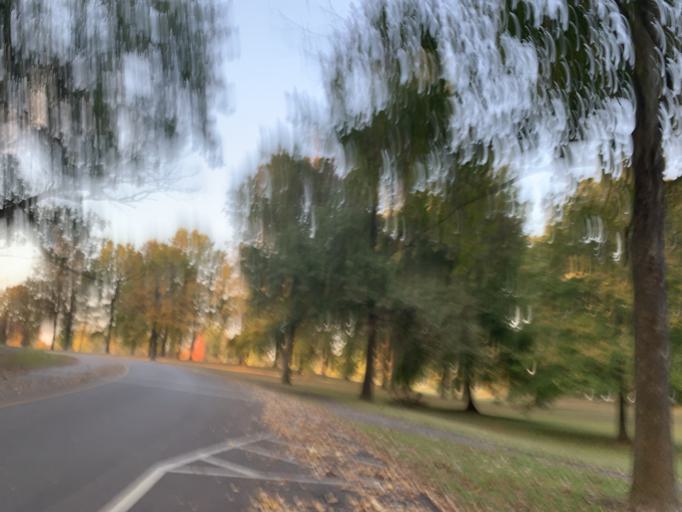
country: US
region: Indiana
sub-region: Floyd County
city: New Albany
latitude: 38.2571
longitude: -85.8264
